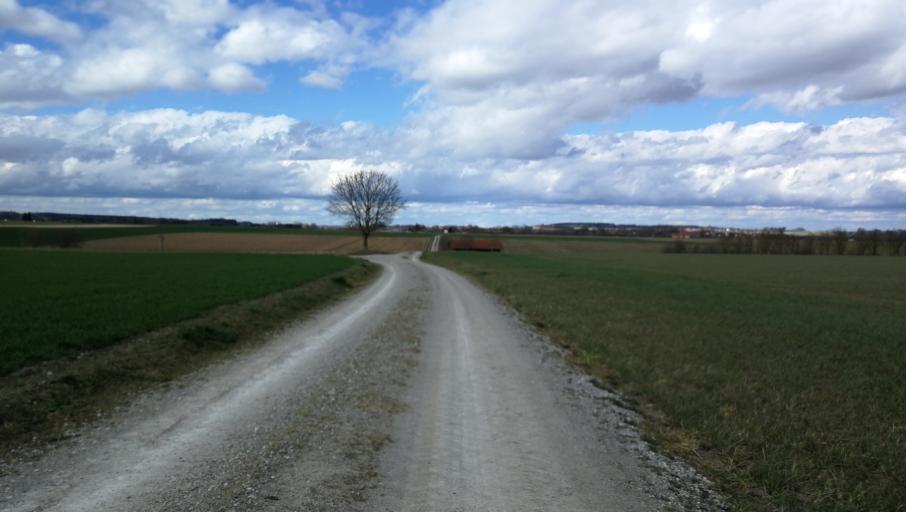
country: DE
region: Bavaria
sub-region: Upper Bavaria
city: Fuerstenfeldbruck
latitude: 48.1951
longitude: 11.2193
